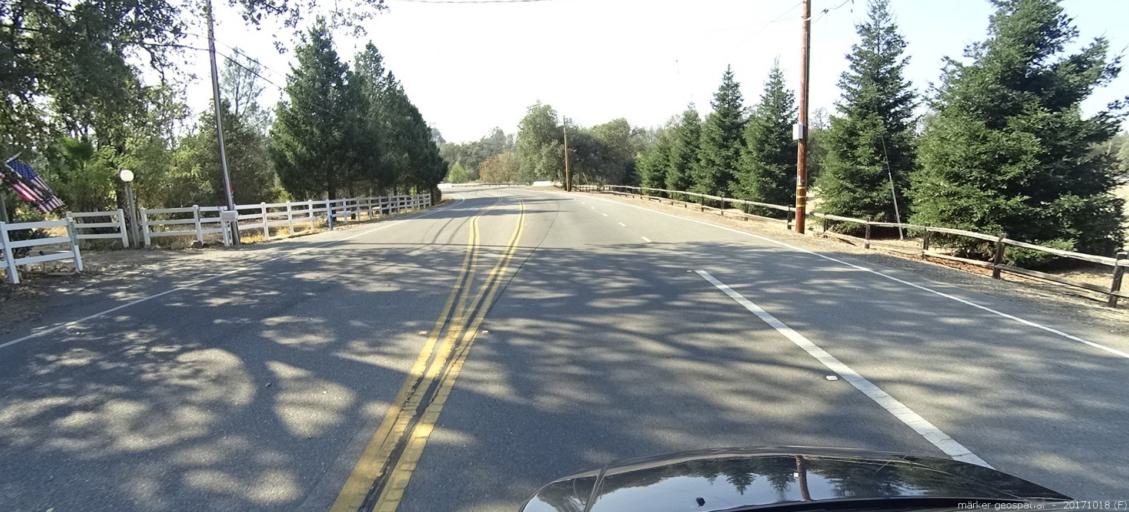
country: US
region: California
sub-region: Shasta County
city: Palo Cedro
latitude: 40.5639
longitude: -122.2880
